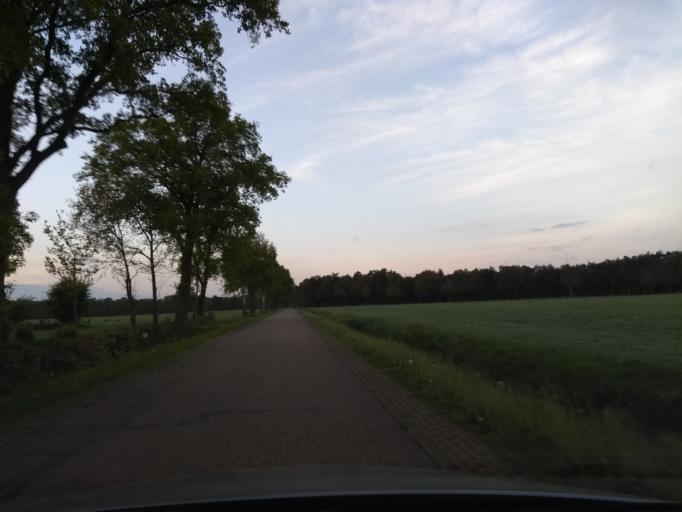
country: NL
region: Overijssel
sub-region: Gemeente Hof van Twente
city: Hengevelde
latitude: 52.2083
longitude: 6.6888
